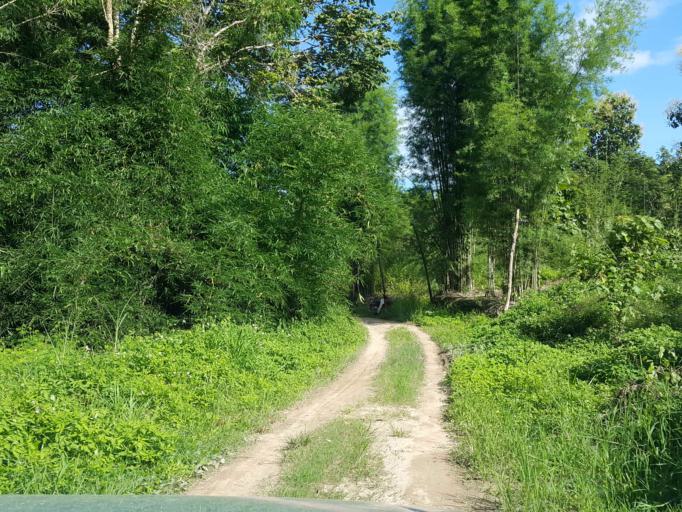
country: TH
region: Chiang Mai
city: Mae Taeng
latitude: 18.9752
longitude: 98.8842
